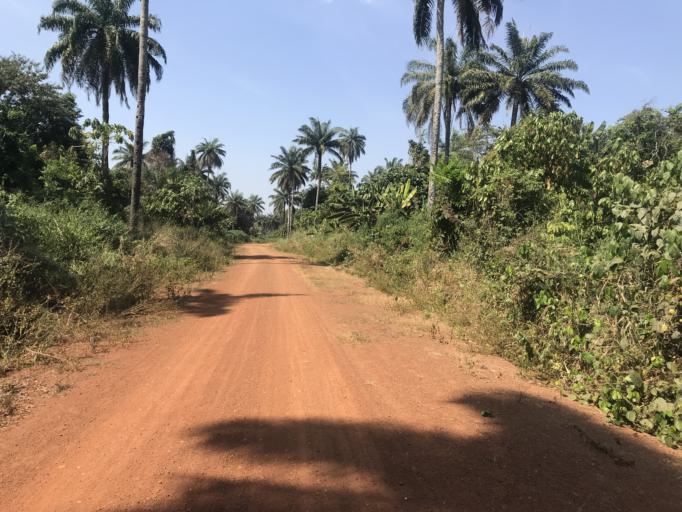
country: NG
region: Osun
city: Ikirun
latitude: 7.9325
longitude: 4.6251
